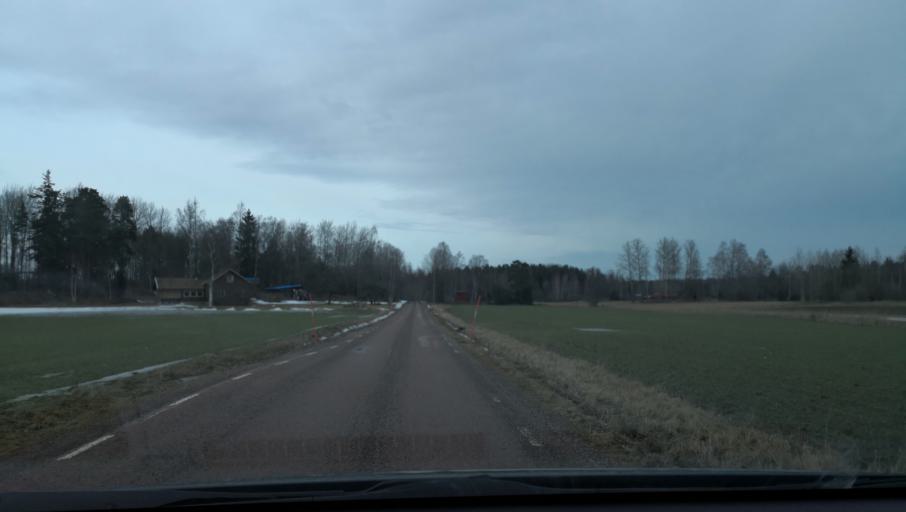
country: SE
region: Vaestmanland
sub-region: Vasteras
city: Skultuna
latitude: 59.6233
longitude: 16.4131
